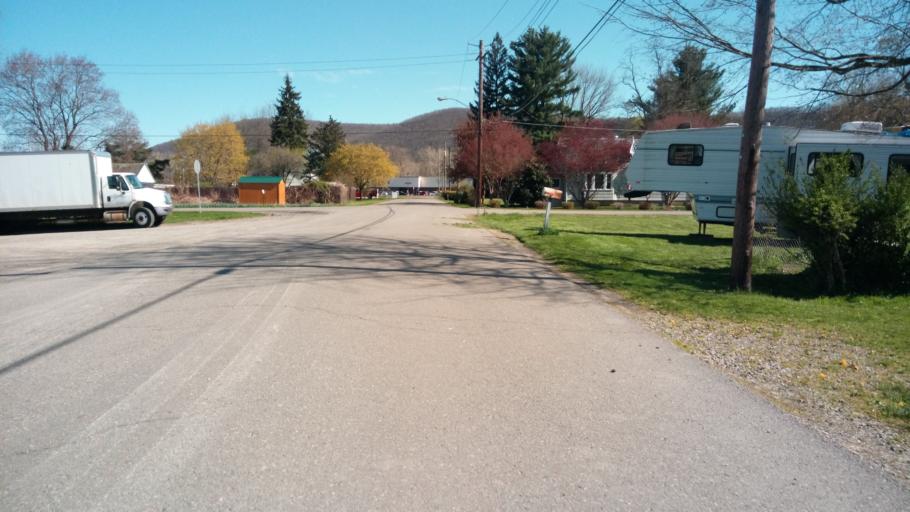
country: US
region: New York
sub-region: Chemung County
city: Southport
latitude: 42.0602
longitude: -76.7946
